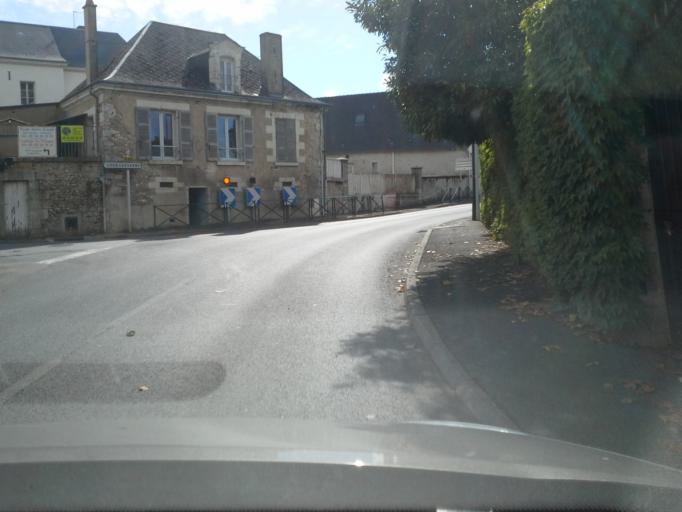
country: FR
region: Centre
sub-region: Departement du Loir-et-Cher
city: Les Montils
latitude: 47.4387
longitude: 1.2961
